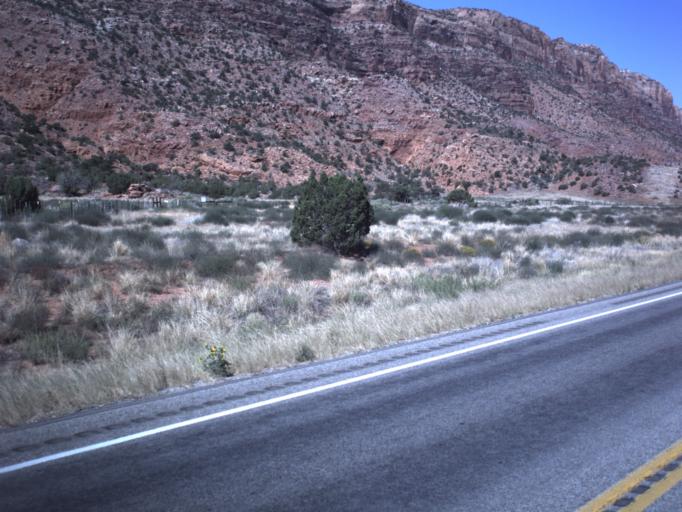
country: US
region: Utah
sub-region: Grand County
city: Moab
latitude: 38.4606
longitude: -109.4438
